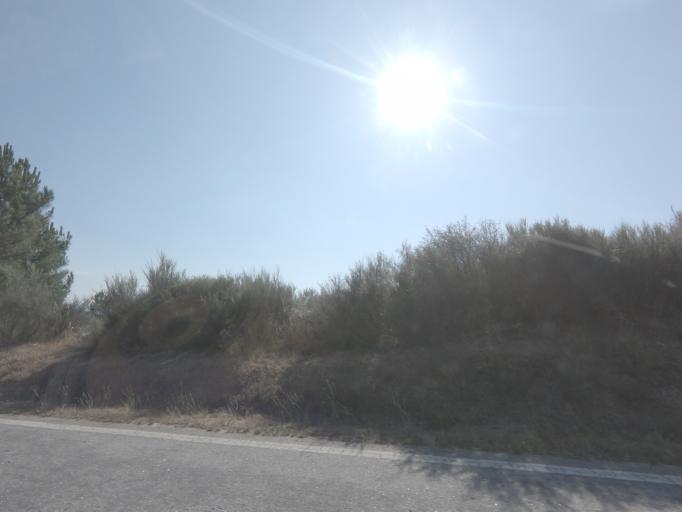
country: PT
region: Viseu
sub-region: Tabuaco
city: Tabuaco
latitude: 41.0626
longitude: -7.5620
